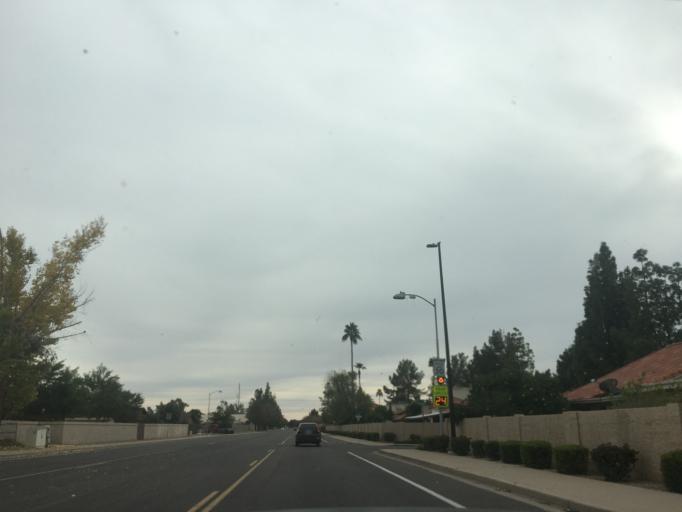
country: US
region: Arizona
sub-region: Maricopa County
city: Gilbert
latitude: 33.3626
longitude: -111.7821
